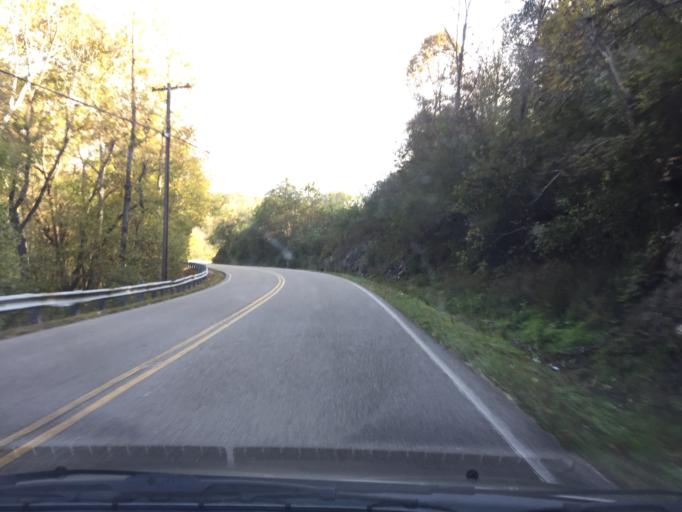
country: US
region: Tennessee
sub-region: Loudon County
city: Loudon
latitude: 35.7082
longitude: -84.3460
